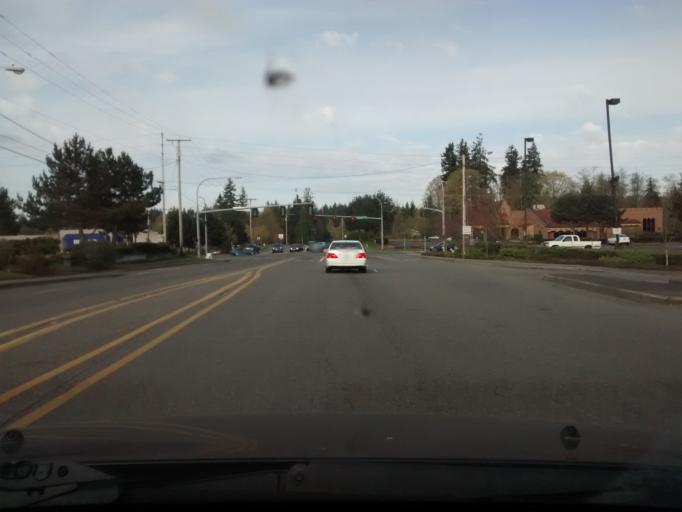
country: US
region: Washington
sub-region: Kitsap County
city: East Port Orchard
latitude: 47.5196
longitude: -122.6298
